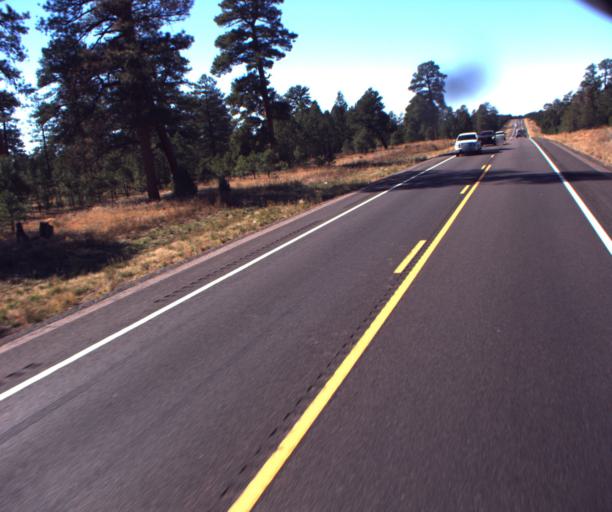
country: US
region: Arizona
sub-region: Apache County
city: Saint Michaels
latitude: 35.7004
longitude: -109.2904
